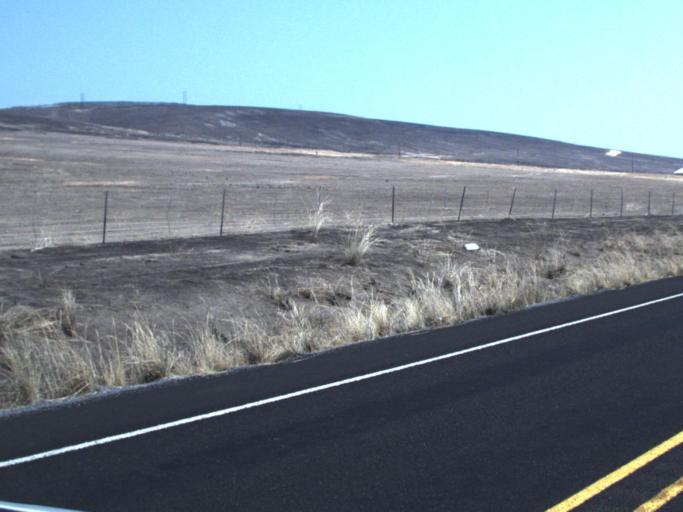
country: US
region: Washington
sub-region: Grant County
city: Desert Aire
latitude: 46.5383
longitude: -119.8596
